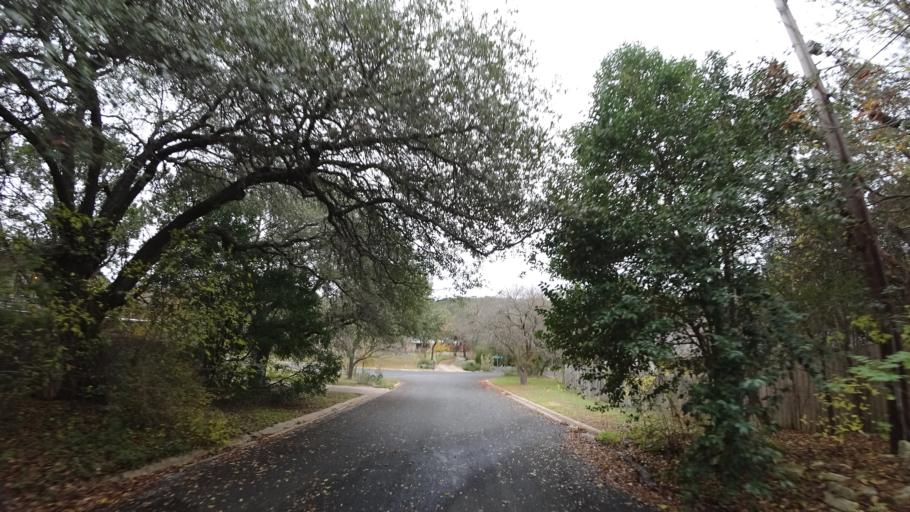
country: US
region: Texas
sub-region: Williamson County
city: Jollyville
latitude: 30.3766
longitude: -97.7859
